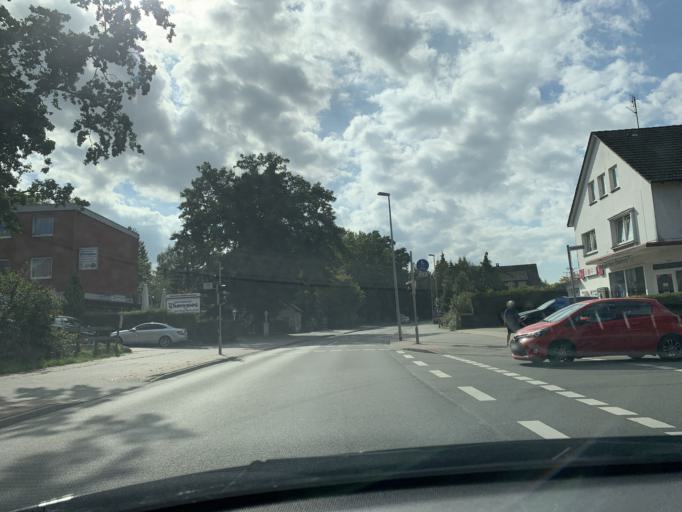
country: DE
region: Lower Saxony
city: Oldenburg
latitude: 53.1280
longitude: 8.1776
